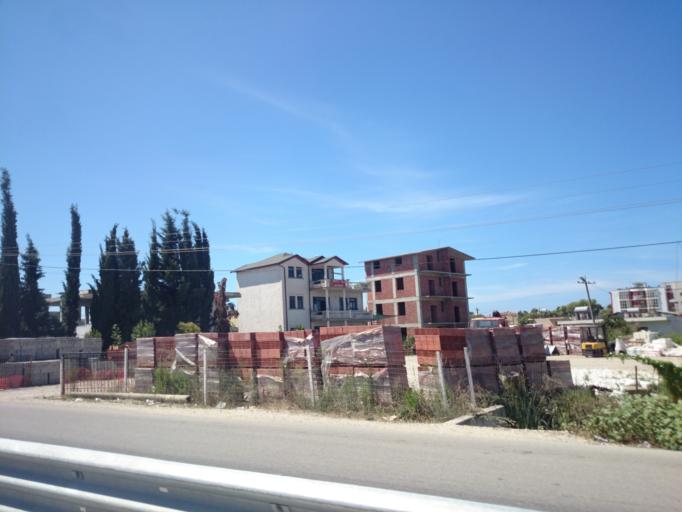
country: AL
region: Tirane
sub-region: Rrethi i Kavajes
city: Golem
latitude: 41.2362
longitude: 19.5240
